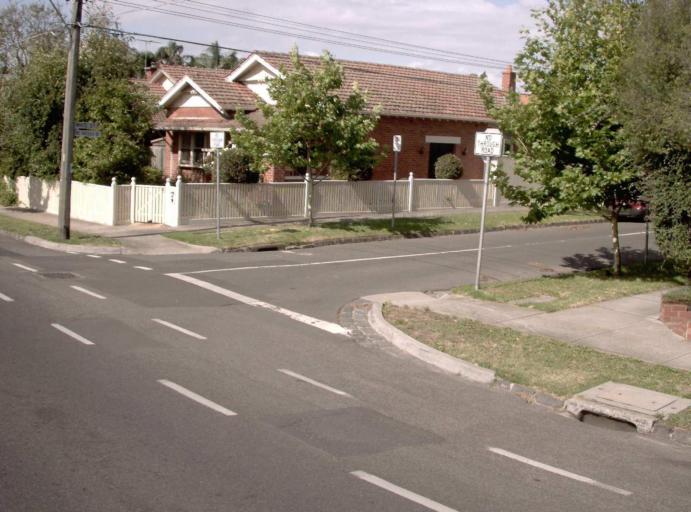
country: AU
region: Victoria
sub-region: Stonnington
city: Malvern East
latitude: -37.8631
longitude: 145.0403
